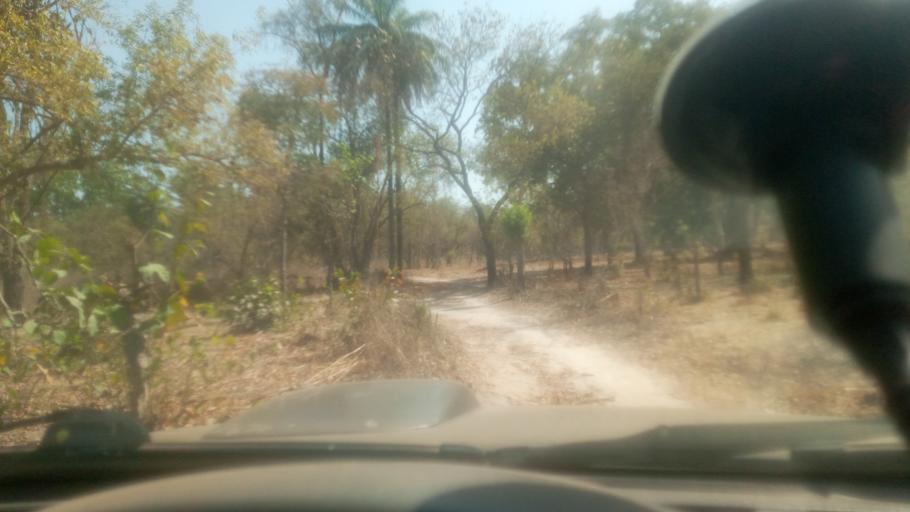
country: GW
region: Oio
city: Farim
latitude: 12.4740
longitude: -15.4067
